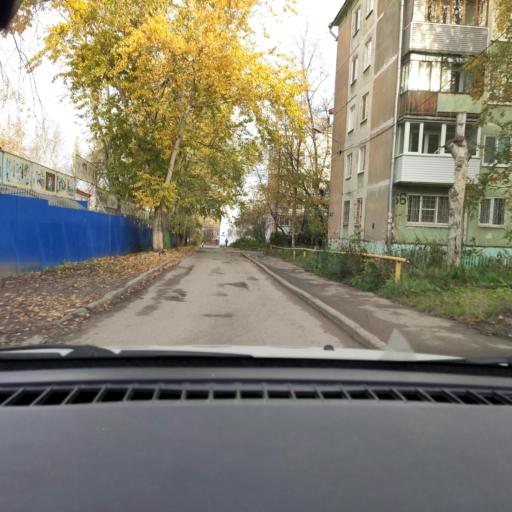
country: RU
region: Perm
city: Perm
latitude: 57.9805
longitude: 56.1898
